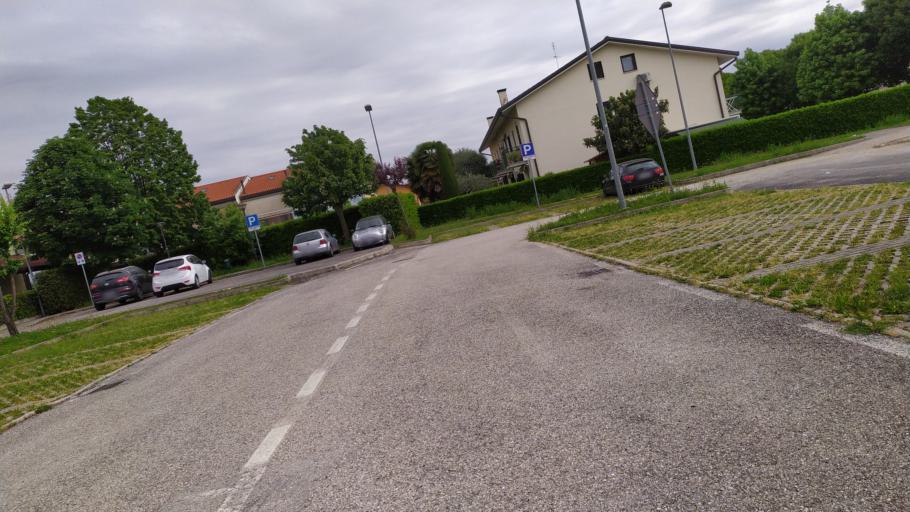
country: IT
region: Veneto
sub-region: Provincia di Padova
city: Camposampiero
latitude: 45.5696
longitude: 11.9275
